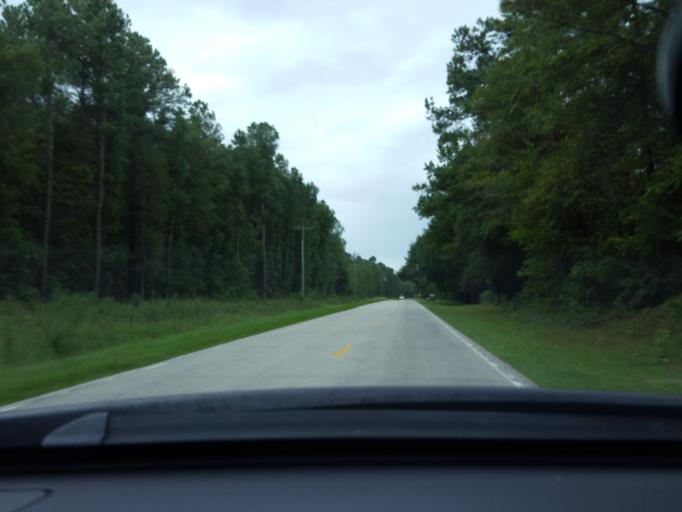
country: US
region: North Carolina
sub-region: Sampson County
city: Clinton
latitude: 34.7825
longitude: -78.3236
